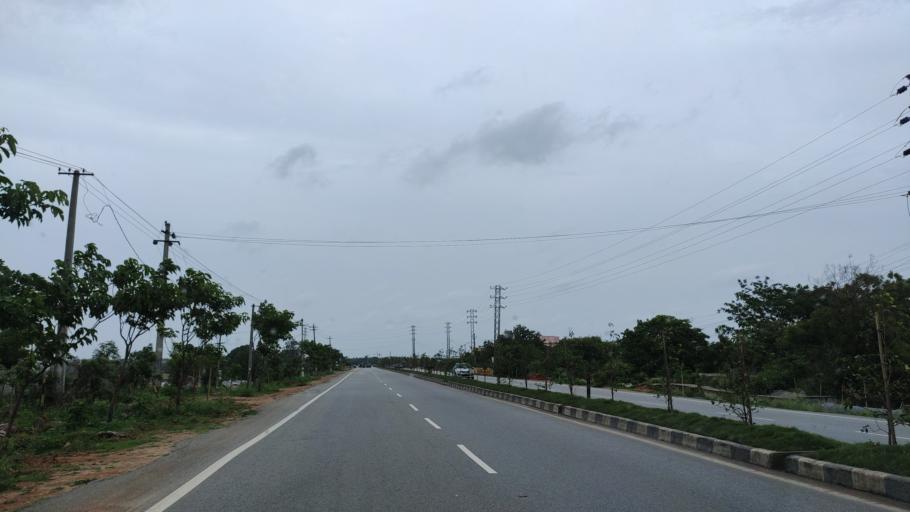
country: IN
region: Telangana
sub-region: Rangareddi
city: Secunderabad
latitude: 17.6040
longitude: 78.5681
